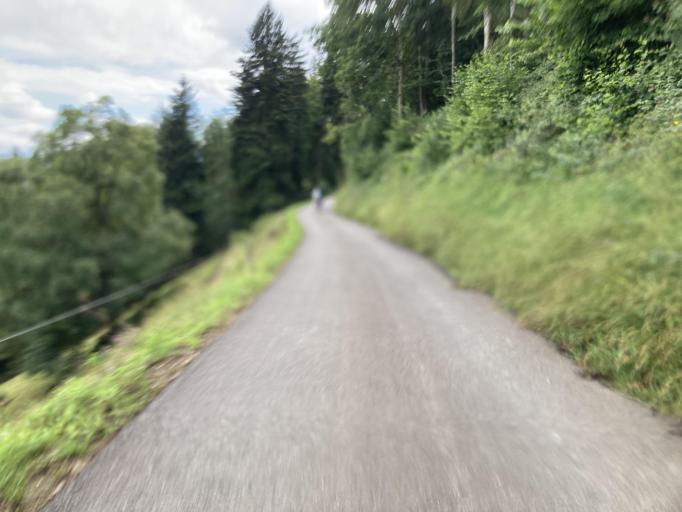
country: CH
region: Thurgau
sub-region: Muenchwilen District
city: Fischingen
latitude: 47.3715
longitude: 8.9435
